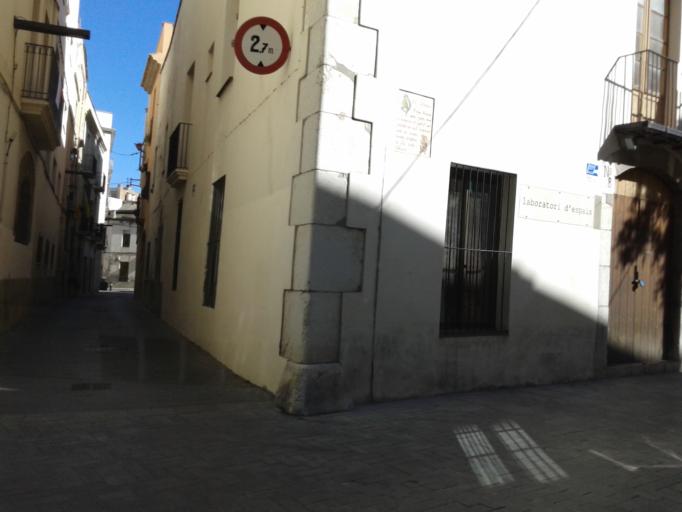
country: ES
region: Catalonia
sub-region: Provincia de Barcelona
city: Vilanova i la Geltru
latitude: 41.2271
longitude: 1.7264
